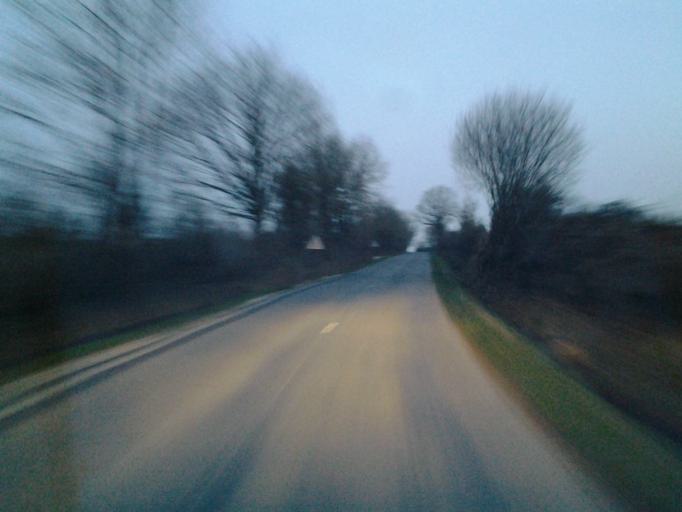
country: FR
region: Pays de la Loire
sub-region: Departement de la Vendee
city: Saint-Florent-des-Bois
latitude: 46.5759
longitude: -1.3465
